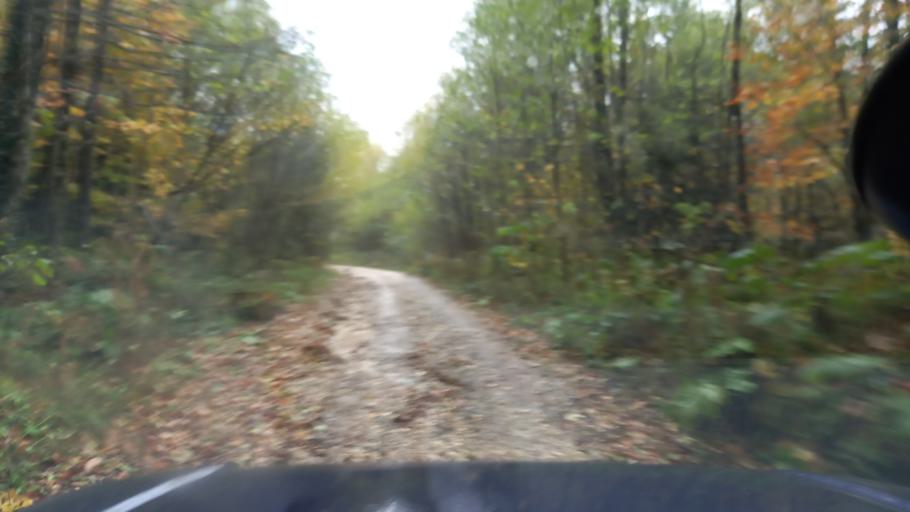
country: RU
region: Krasnodarskiy
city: Neftegorsk
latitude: 44.0299
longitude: 39.8365
